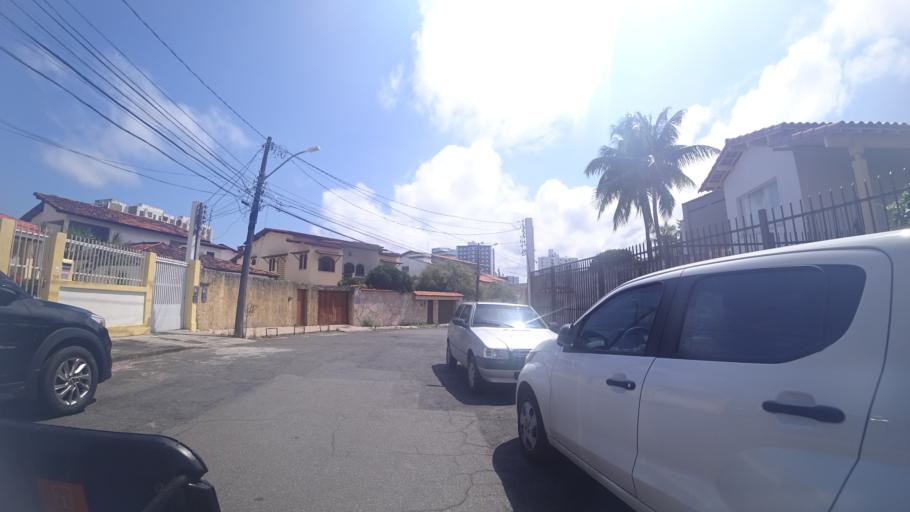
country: BR
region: Bahia
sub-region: Salvador
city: Salvador
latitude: -12.9930
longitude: -38.4592
